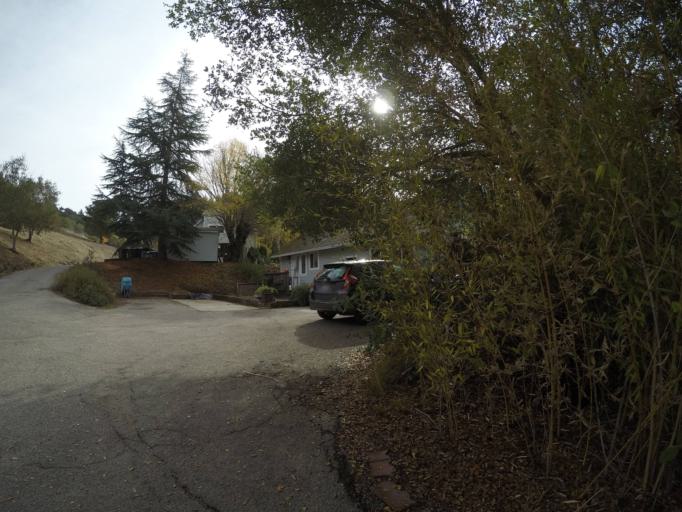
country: US
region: California
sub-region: Santa Cruz County
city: Scotts Valley
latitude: 37.0314
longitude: -121.9823
